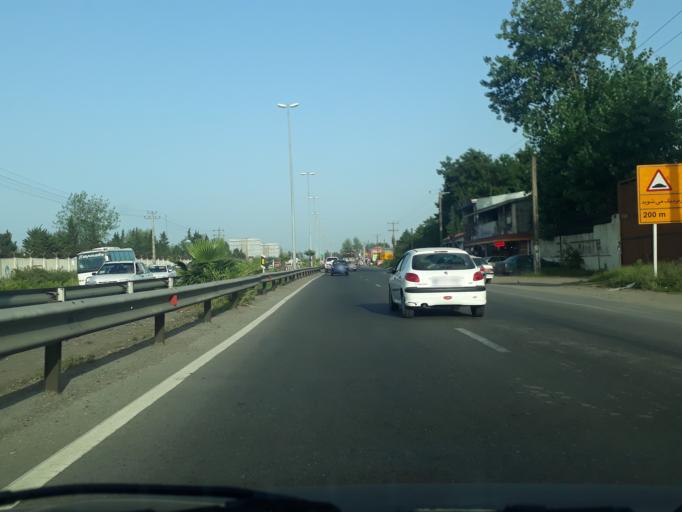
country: IR
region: Gilan
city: Bandar-e Anzali
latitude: 37.4579
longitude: 49.6061
